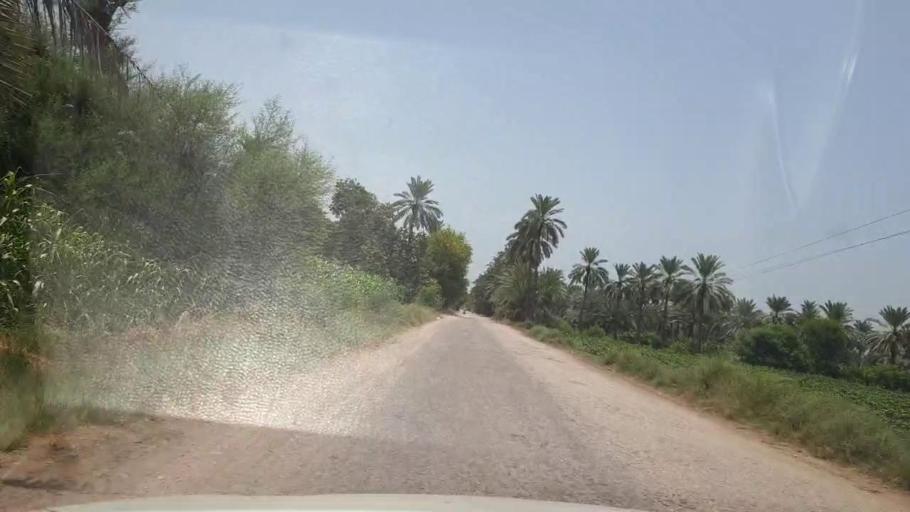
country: PK
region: Sindh
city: Bozdar
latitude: 27.1887
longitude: 68.5973
